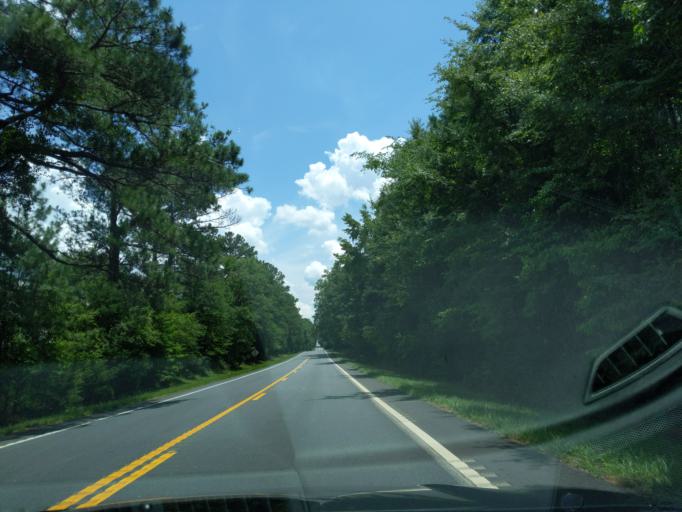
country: US
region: South Carolina
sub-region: Edgefield County
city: Edgefield
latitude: 33.8513
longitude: -81.9810
